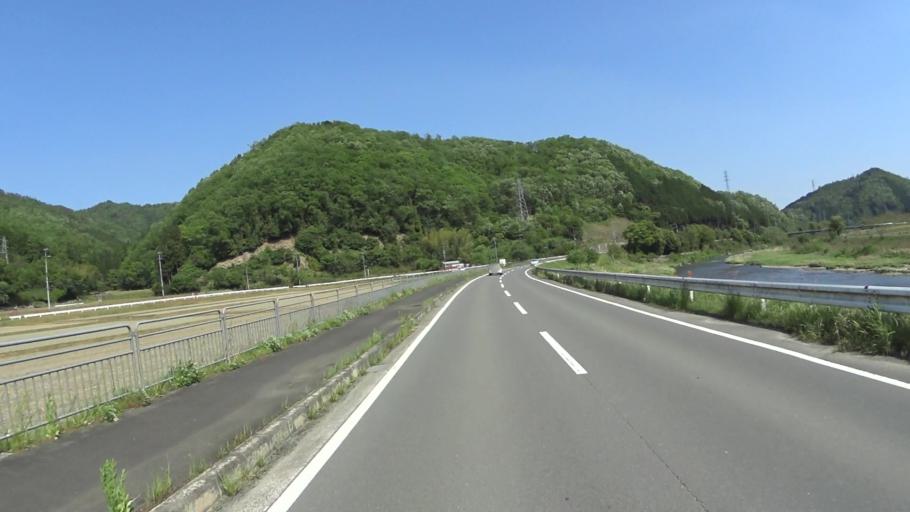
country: JP
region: Kyoto
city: Kameoka
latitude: 35.1257
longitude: 135.5028
